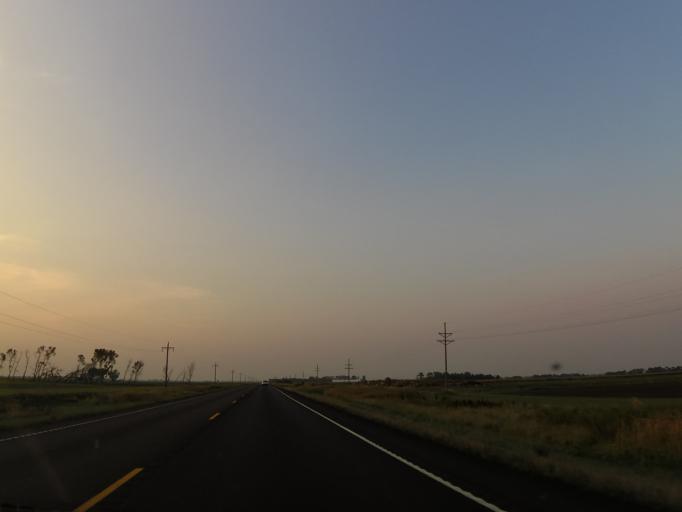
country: US
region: North Dakota
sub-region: Walsh County
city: Park River
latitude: 48.2141
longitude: -97.6221
